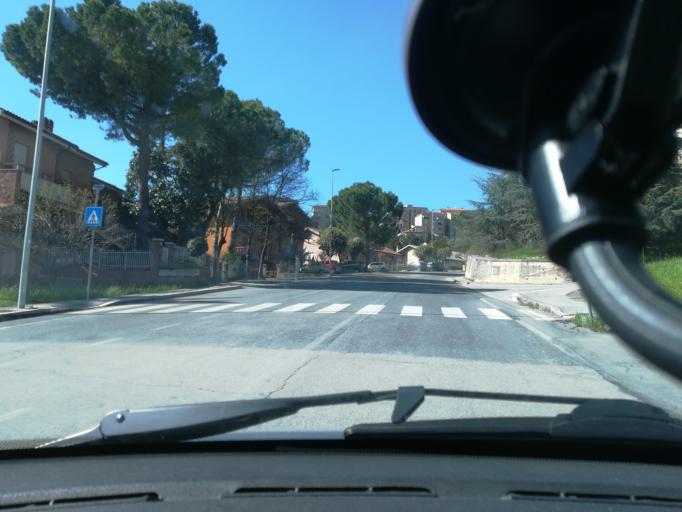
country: IT
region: The Marches
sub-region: Provincia di Macerata
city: Macerata
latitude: 43.2935
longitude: 13.4502
